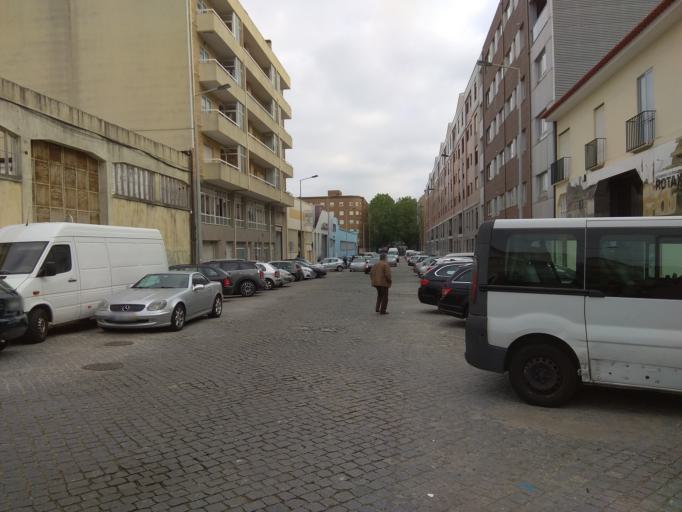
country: PT
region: Porto
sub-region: Matosinhos
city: Matosinhos
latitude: 41.1755
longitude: -8.6830
